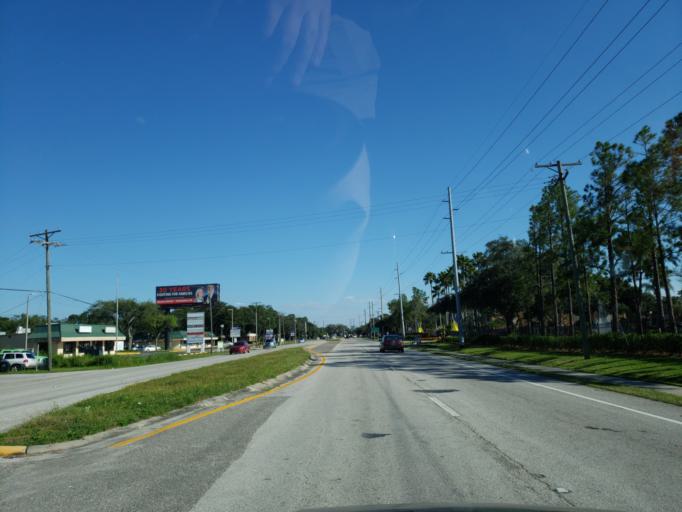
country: US
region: Florida
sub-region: Hillsborough County
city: Carrollwood Village
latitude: 28.0457
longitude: -82.5157
